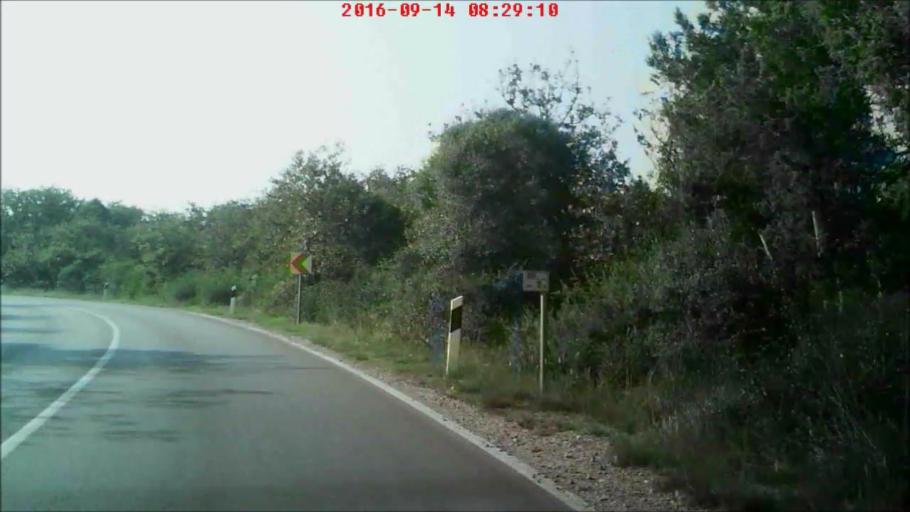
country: HR
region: Zadarska
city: Zadar
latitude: 44.1810
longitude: 15.2811
